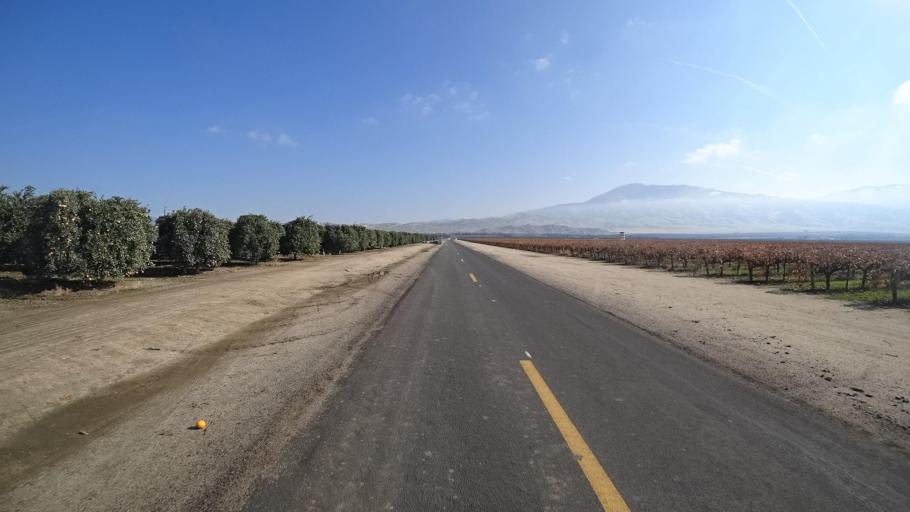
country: US
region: California
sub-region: Kern County
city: Arvin
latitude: 35.2675
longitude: -118.7781
